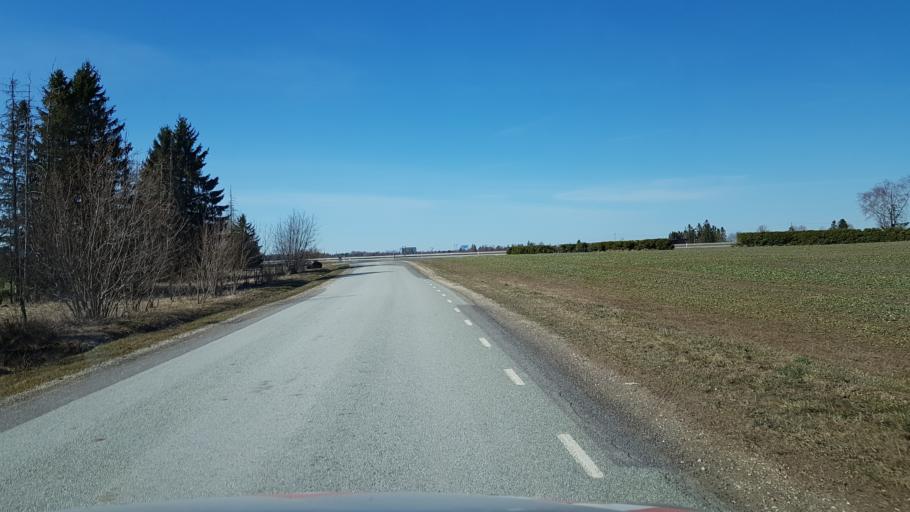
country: EE
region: Laeaene-Virumaa
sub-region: Someru vald
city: Someru
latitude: 59.3645
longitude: 26.4629
